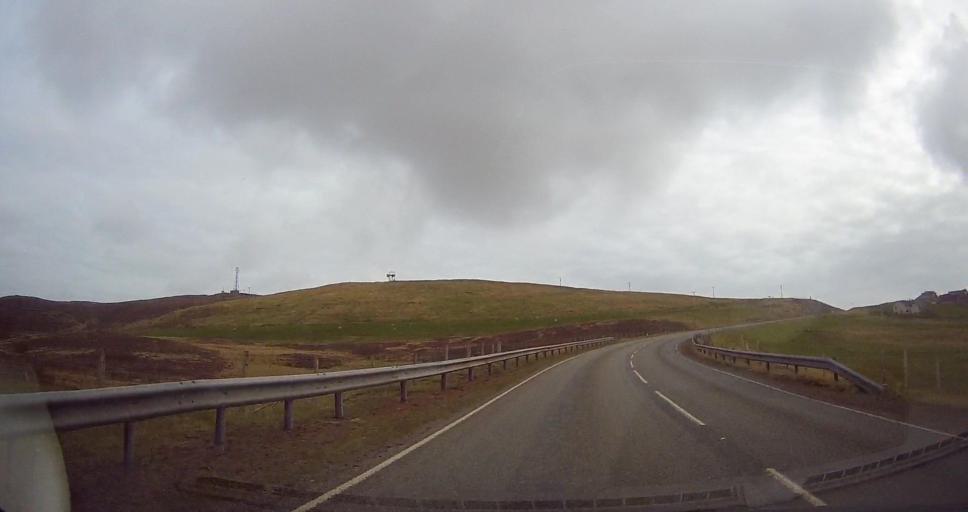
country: GB
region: Scotland
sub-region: Shetland Islands
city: Lerwick
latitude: 60.1383
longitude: -1.2119
